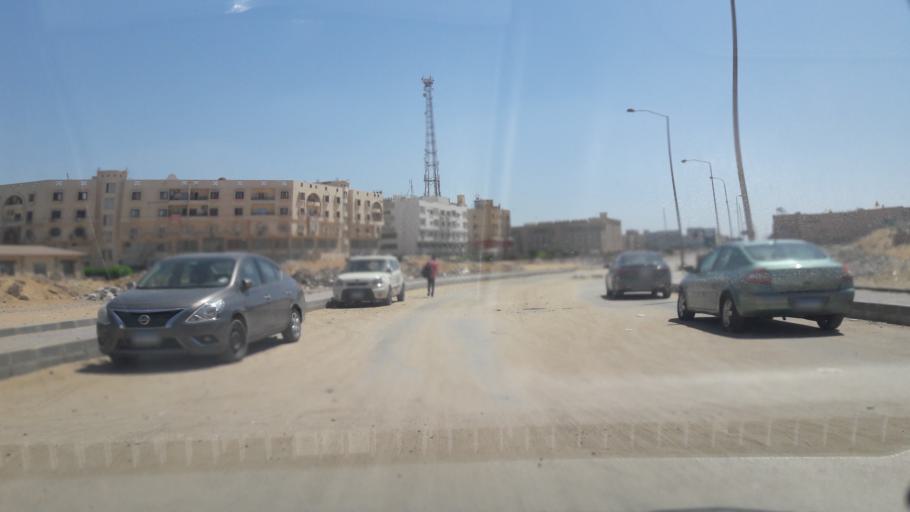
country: EG
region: Al Jizah
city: Madinat Sittah Uktubar
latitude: 29.9652
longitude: 30.9314
